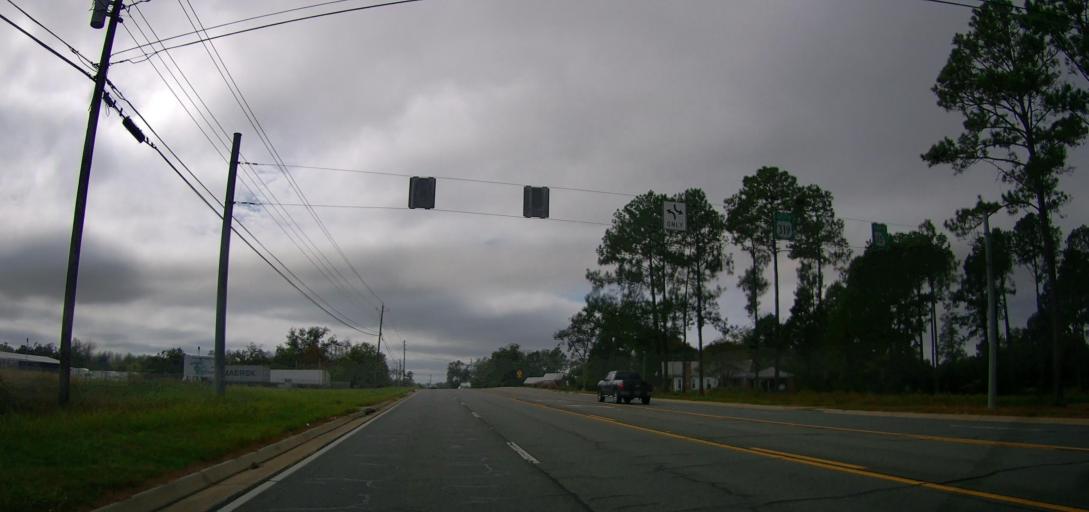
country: US
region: Georgia
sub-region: Colquitt County
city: Moultrie
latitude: 31.2183
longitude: -83.7665
